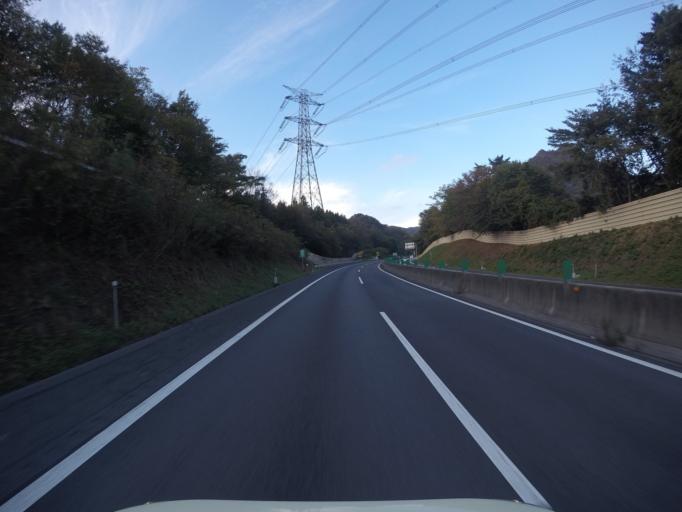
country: JP
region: Gunma
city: Annaka
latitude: 36.3239
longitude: 138.6892
